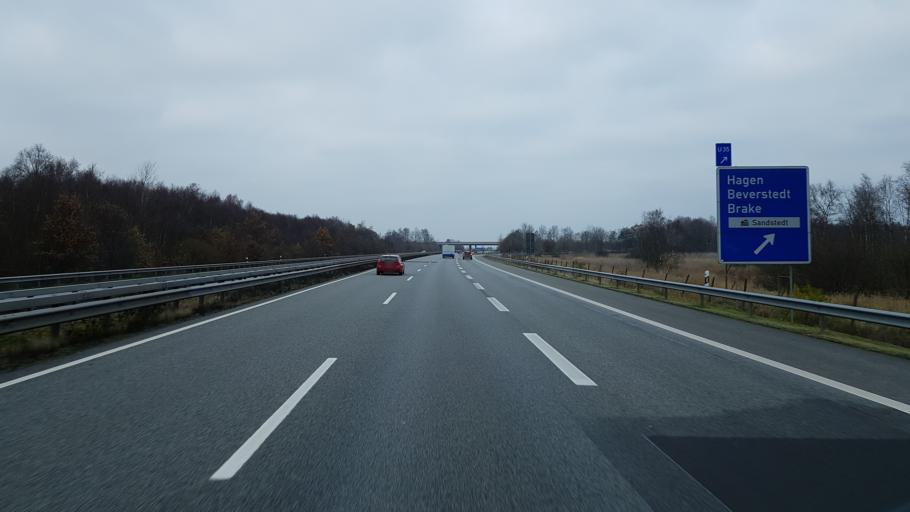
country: DE
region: Lower Saxony
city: Driftsethe
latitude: 53.3657
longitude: 8.5798
